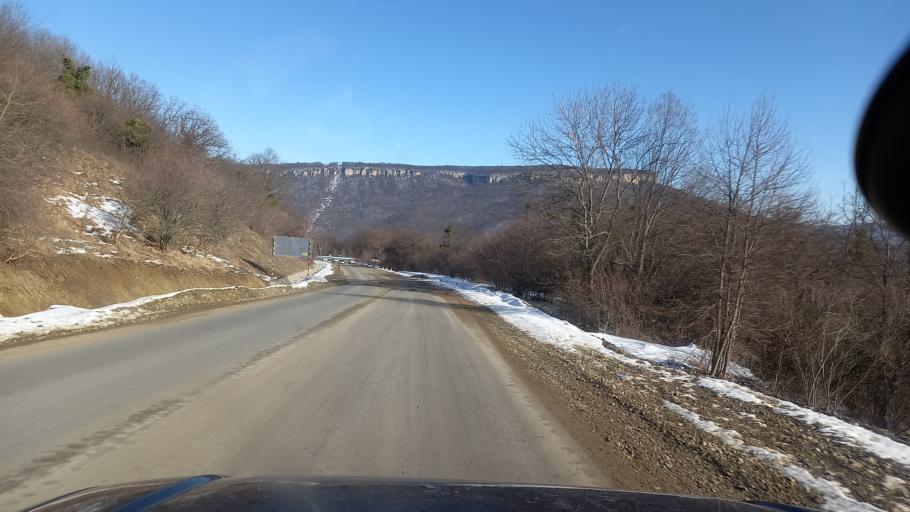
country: RU
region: Adygeya
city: Kamennomostskiy
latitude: 44.2401
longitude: 40.1785
